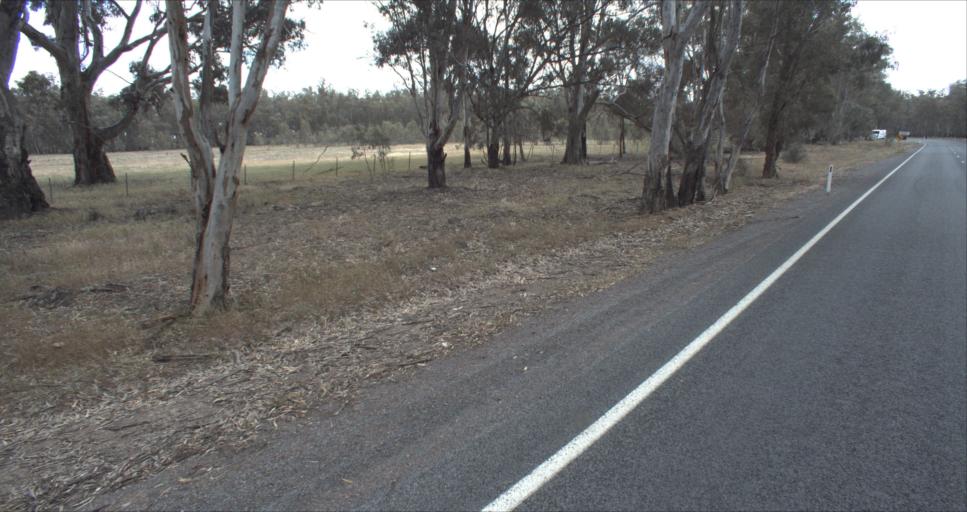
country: AU
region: New South Wales
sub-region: Leeton
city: Leeton
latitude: -34.6410
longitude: 146.3632
